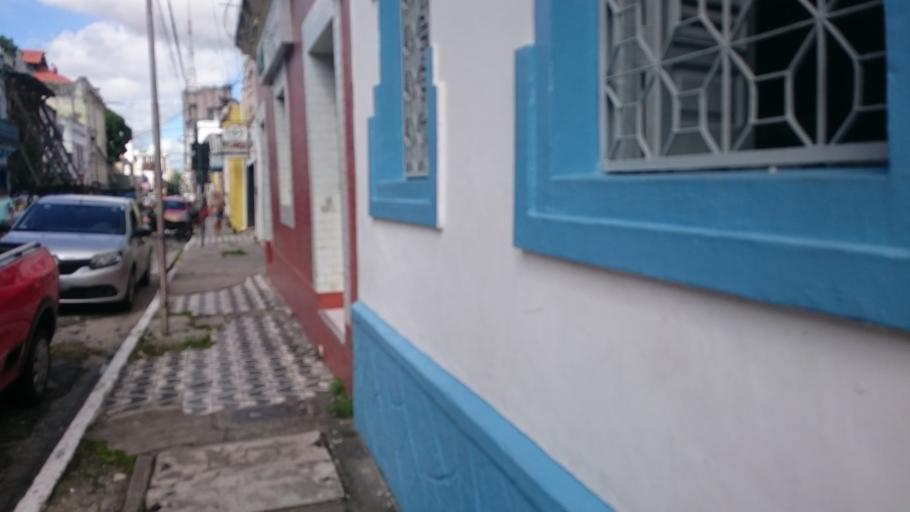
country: BR
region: Paraiba
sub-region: Joao Pessoa
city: Joao Pessoa
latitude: -7.1166
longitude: -34.8836
